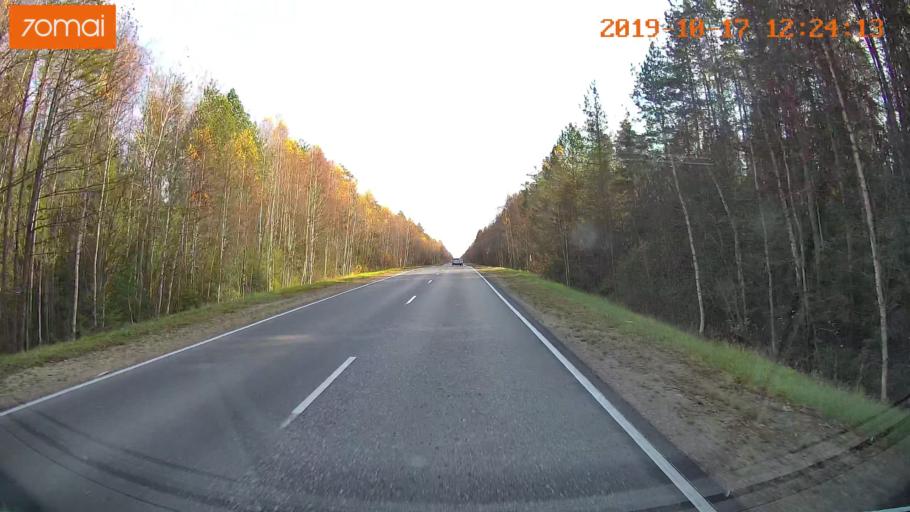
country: RU
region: Rjazan
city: Gus'-Zheleznyy
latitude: 55.0373
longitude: 41.2103
